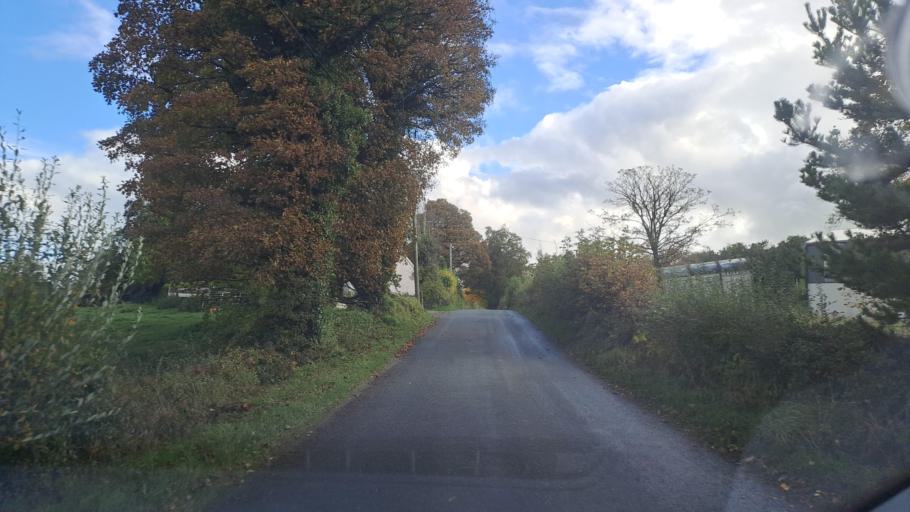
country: IE
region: Ulster
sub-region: An Cabhan
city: Bailieborough
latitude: 53.9900
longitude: -7.0053
